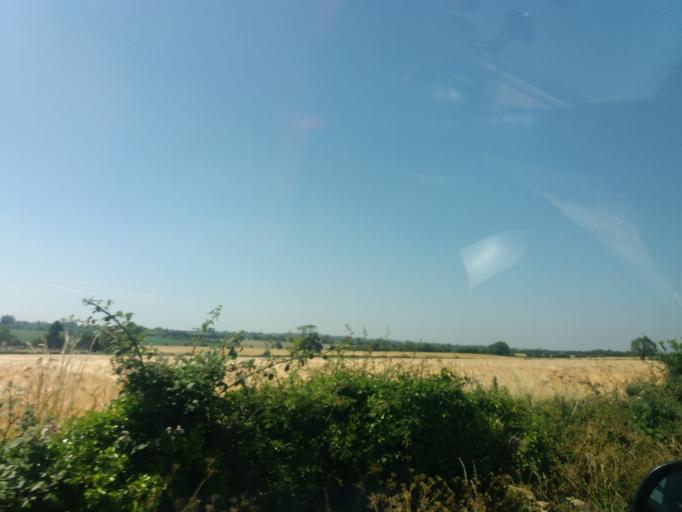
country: IE
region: Leinster
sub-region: An Mhi
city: Ashbourne
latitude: 53.5465
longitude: -6.3252
